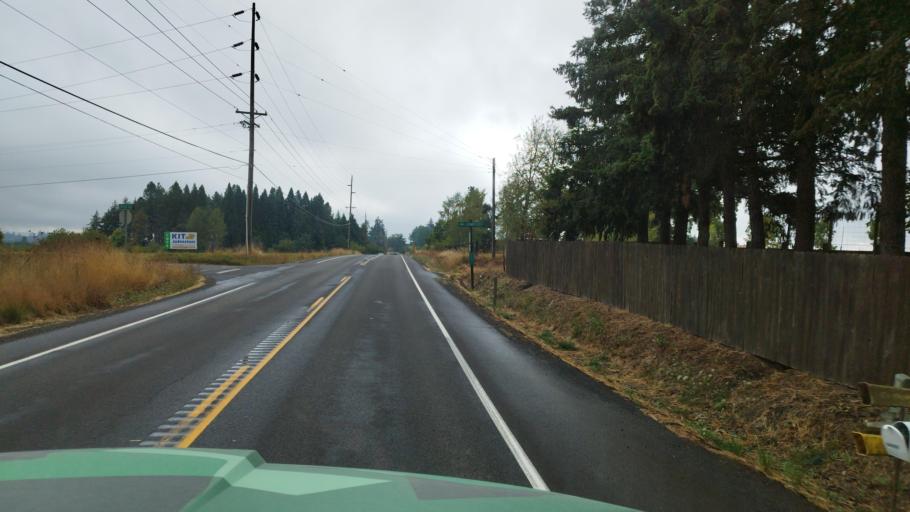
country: US
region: Oregon
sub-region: Yamhill County
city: Yamhill
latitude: 45.3218
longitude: -123.1776
